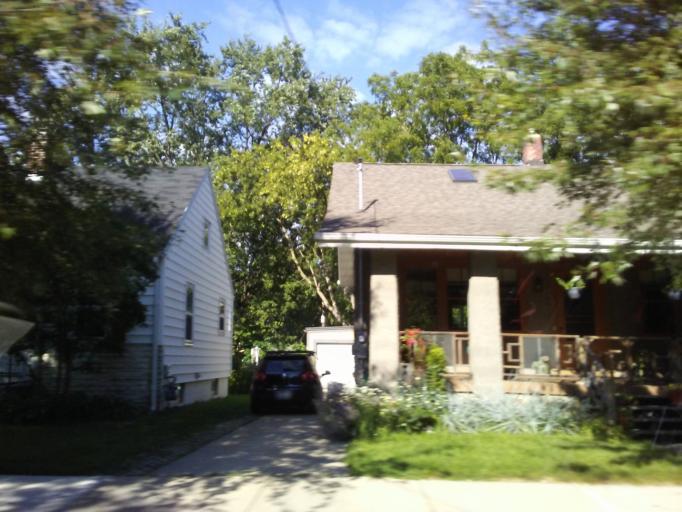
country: US
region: Wisconsin
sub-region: Dane County
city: Monona
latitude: 43.0984
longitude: -89.3441
